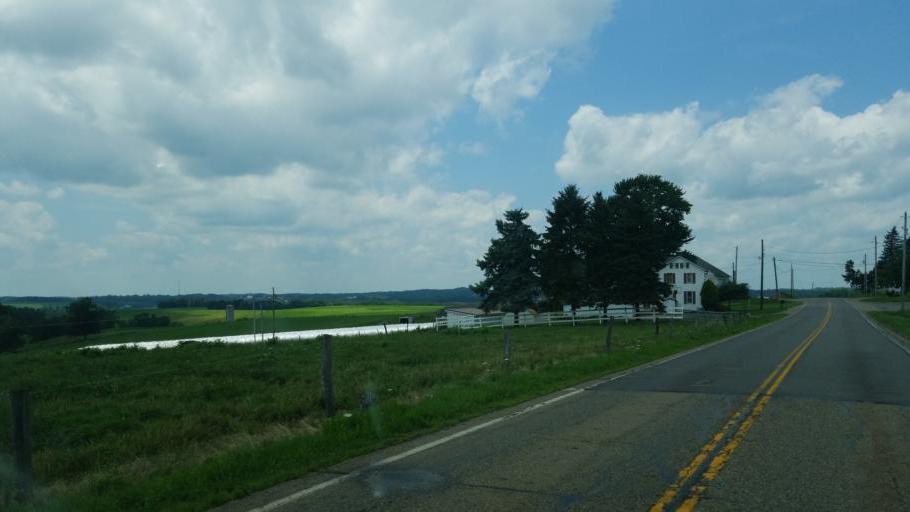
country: US
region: Ohio
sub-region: Stark County
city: Minerva
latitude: 40.7912
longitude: -81.0498
